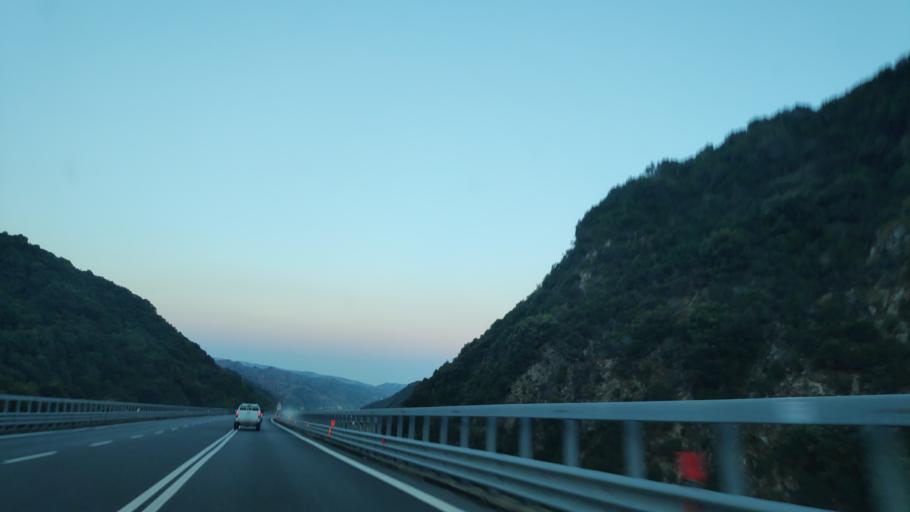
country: IT
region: Calabria
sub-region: Provincia di Reggio Calabria
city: Mammola
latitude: 38.3623
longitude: 16.1936
